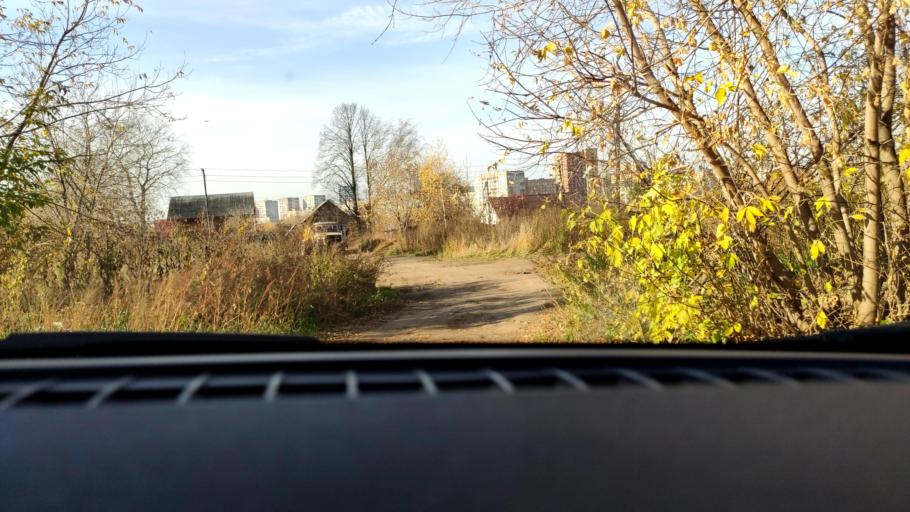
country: RU
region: Perm
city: Perm
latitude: 58.0301
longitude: 56.3209
